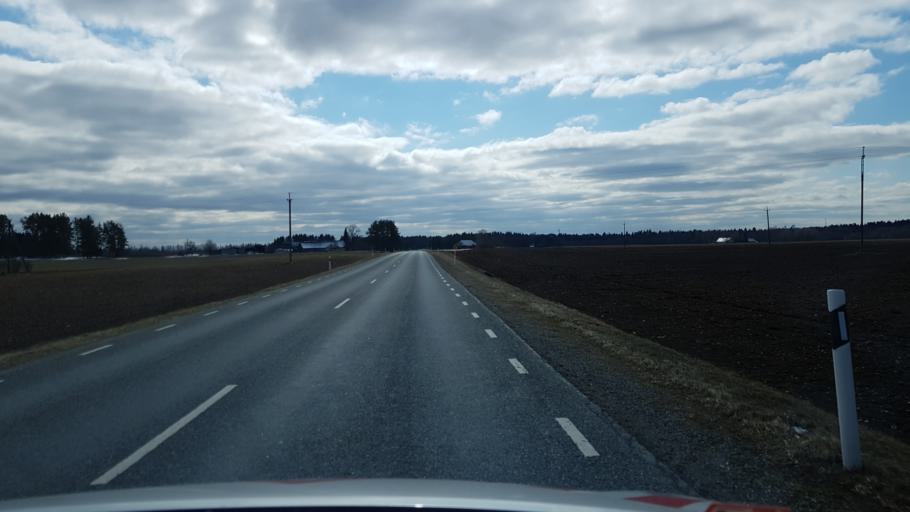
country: EE
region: Laeaene-Virumaa
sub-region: Tapa vald
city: Tapa
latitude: 59.2968
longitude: 25.9987
